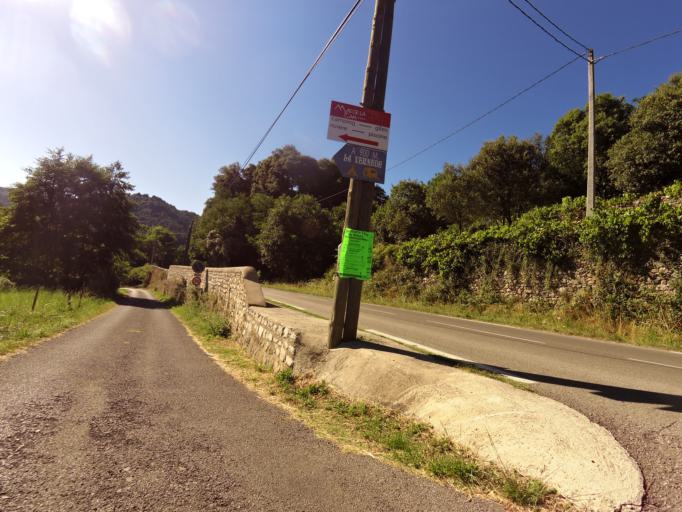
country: FR
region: Languedoc-Roussillon
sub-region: Departement du Gard
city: Saint-Jean-du-Gard
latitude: 44.1136
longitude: 3.8558
